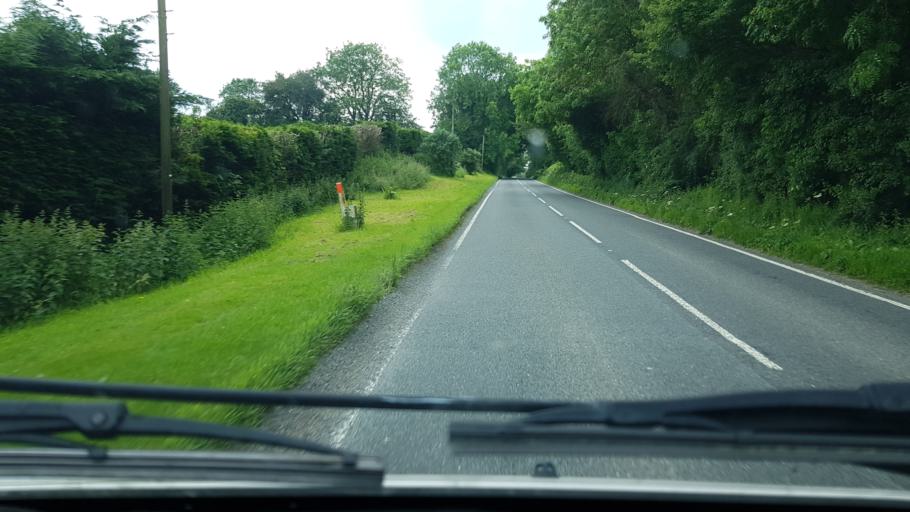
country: GB
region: England
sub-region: Gloucestershire
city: Stow on the Wold
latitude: 51.9413
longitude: -1.7287
